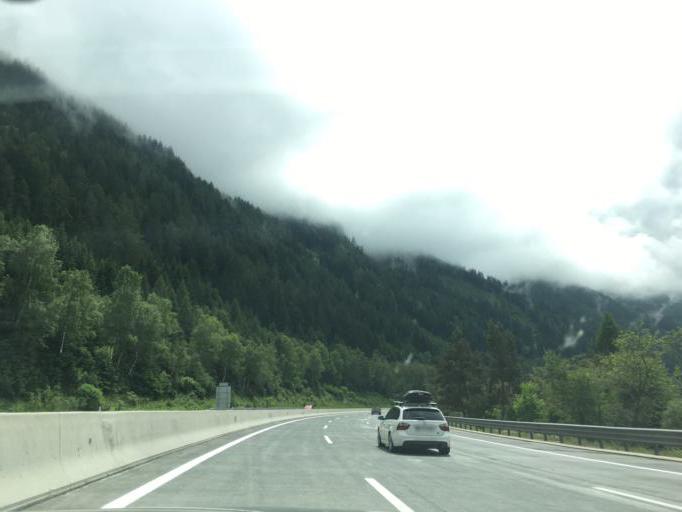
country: AT
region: Salzburg
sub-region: Politischer Bezirk Tamsweg
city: Sankt Michael im Lungau
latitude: 47.0863
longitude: 13.6066
